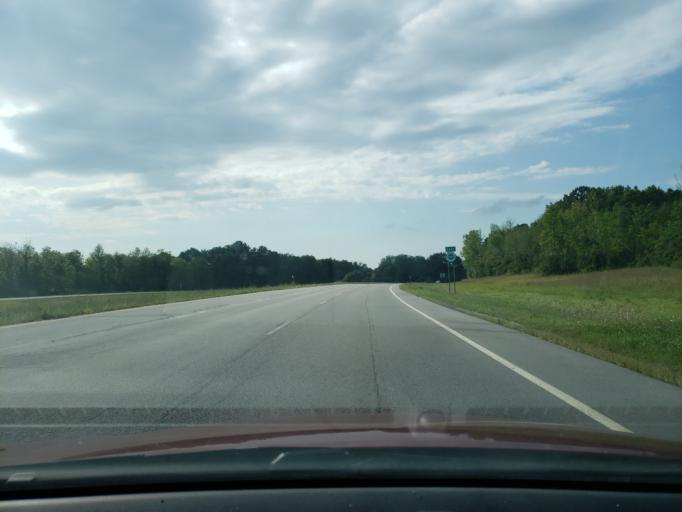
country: US
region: New York
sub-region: Monroe County
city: Greece
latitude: 43.2727
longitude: -77.6875
